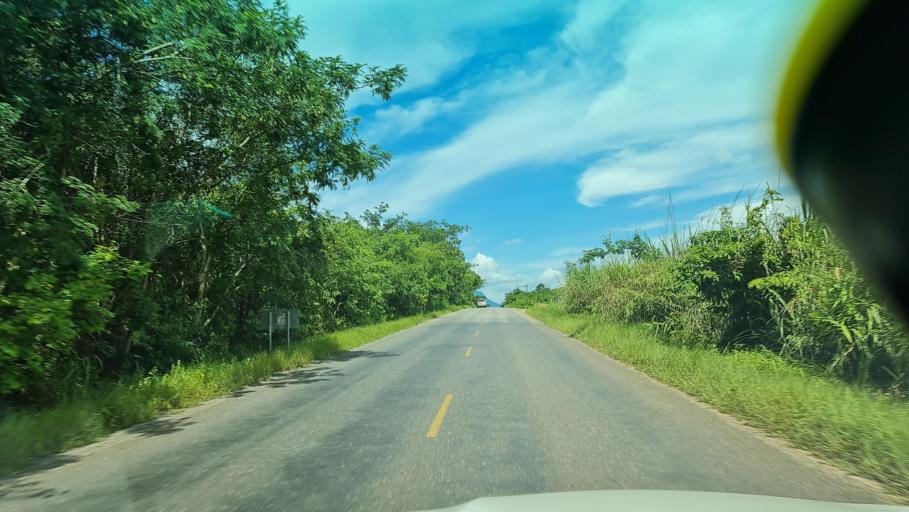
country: LA
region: Bolikhamxai
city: Ban Nahin
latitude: 18.2838
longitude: 104.1431
